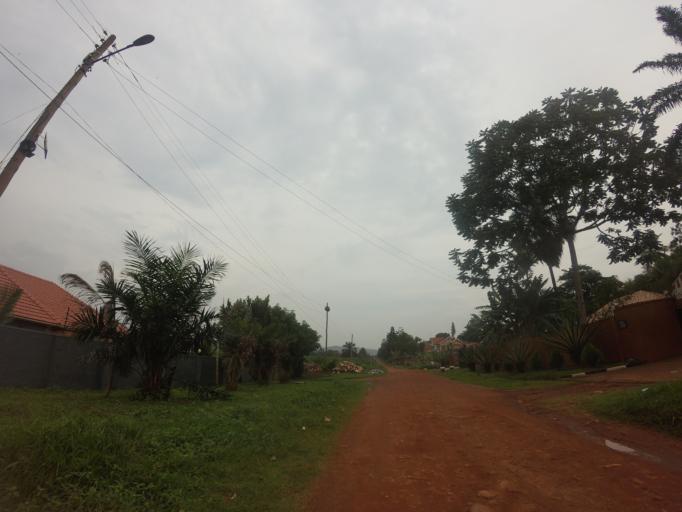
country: UG
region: Central Region
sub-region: Wakiso District
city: Kireka
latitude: 0.3550
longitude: 32.6218
